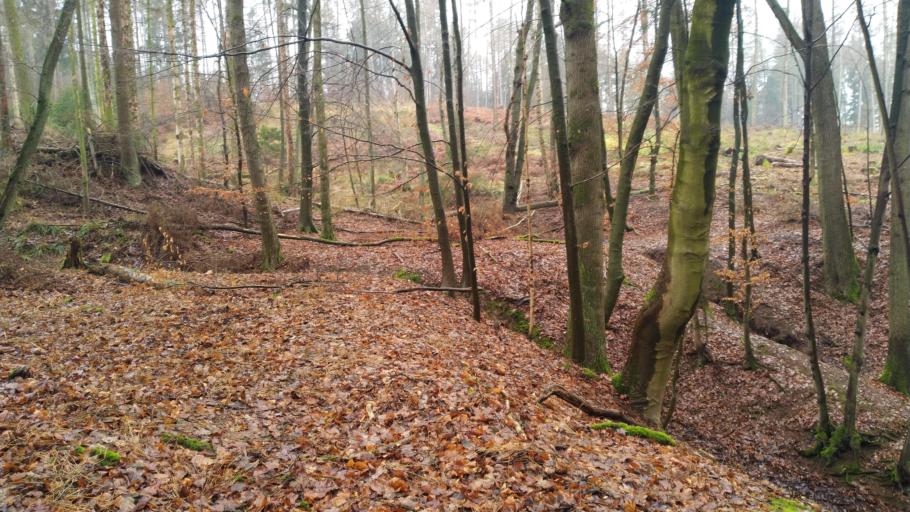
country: DE
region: Lower Saxony
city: Bad Salzdetfurth
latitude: 52.0817
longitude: 9.9744
